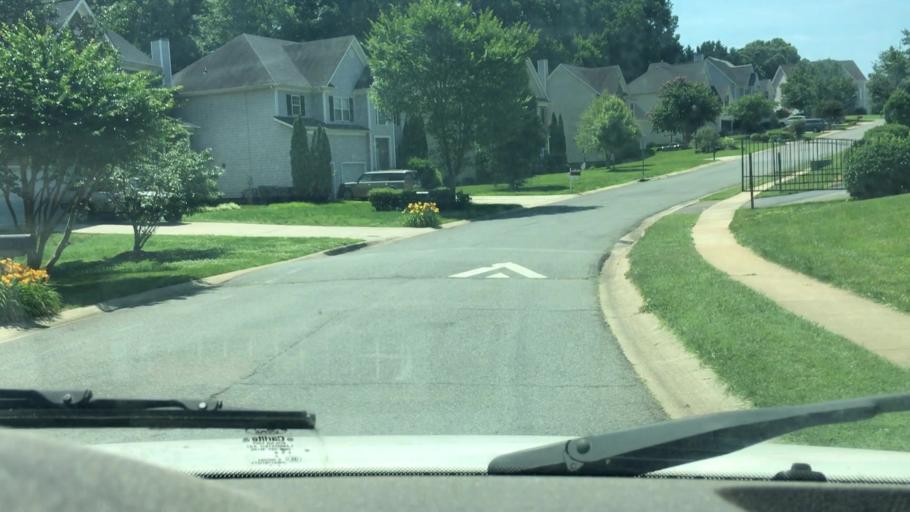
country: US
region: North Carolina
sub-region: Mecklenburg County
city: Huntersville
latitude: 35.4454
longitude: -80.8507
